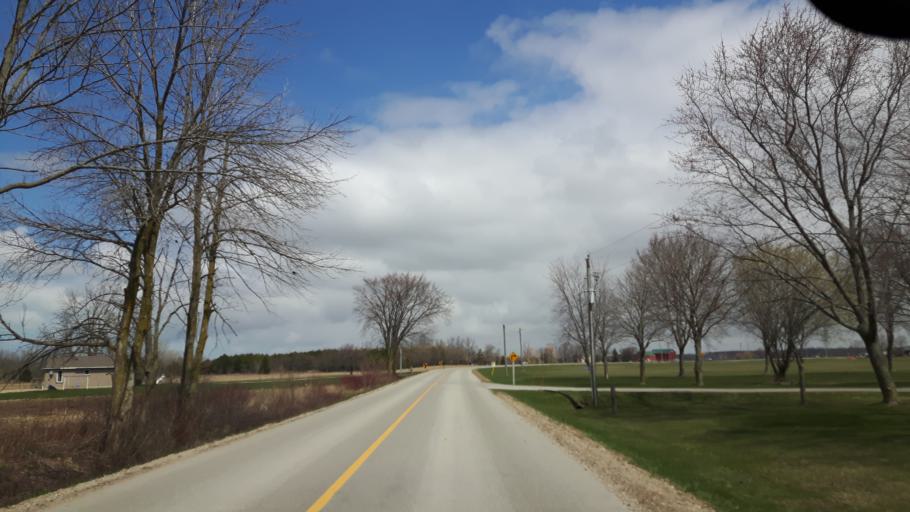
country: CA
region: Ontario
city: Goderich
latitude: 43.7077
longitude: -81.6645
